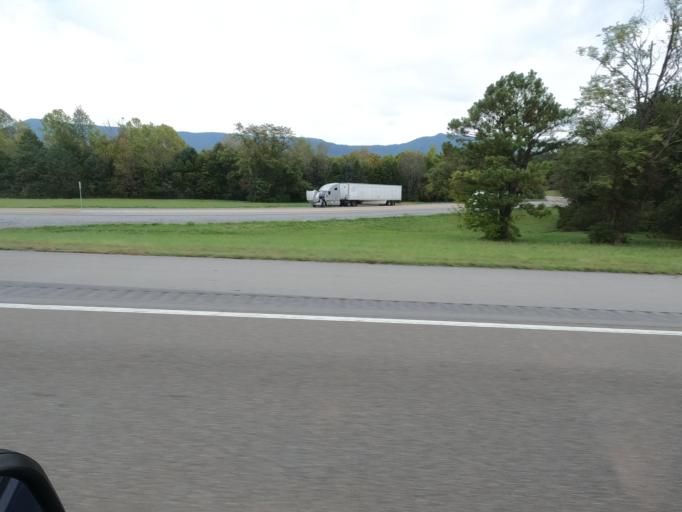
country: US
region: Tennessee
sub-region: Washington County
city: Fall Branch
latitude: 36.3583
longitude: -82.7019
